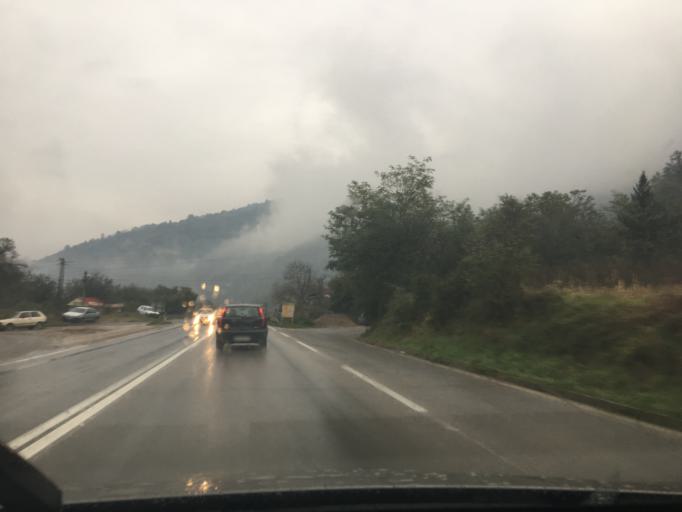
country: RS
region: Central Serbia
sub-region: Pcinjski Okrug
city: Vladicin Han
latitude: 42.7737
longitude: 22.0914
